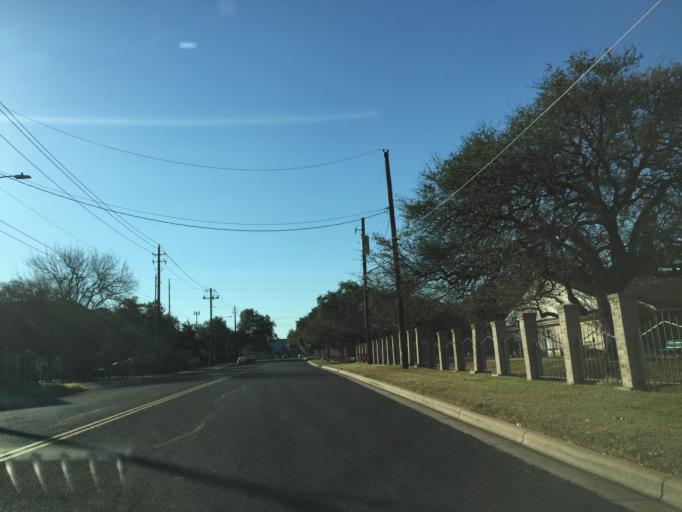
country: US
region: Texas
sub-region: Williamson County
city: Jollyville
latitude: 30.4391
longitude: -97.7613
